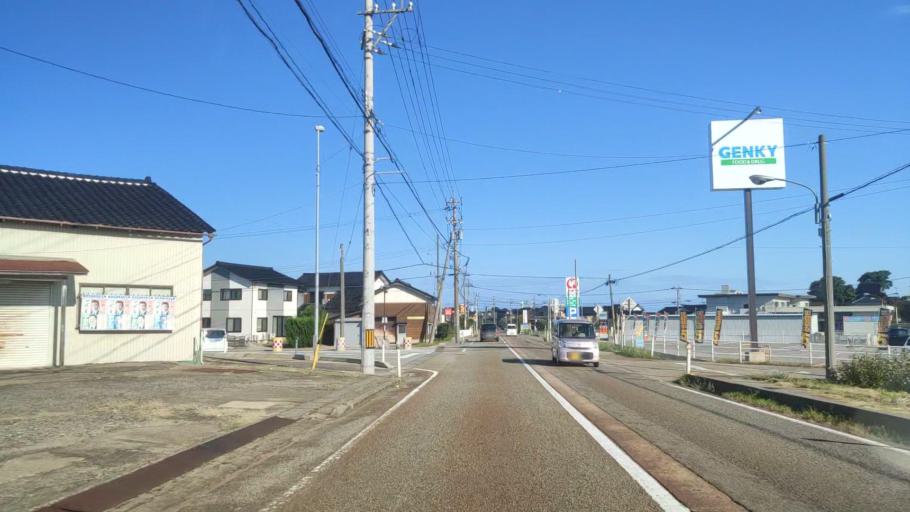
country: JP
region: Ishikawa
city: Hakui
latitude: 36.8195
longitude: 136.7577
